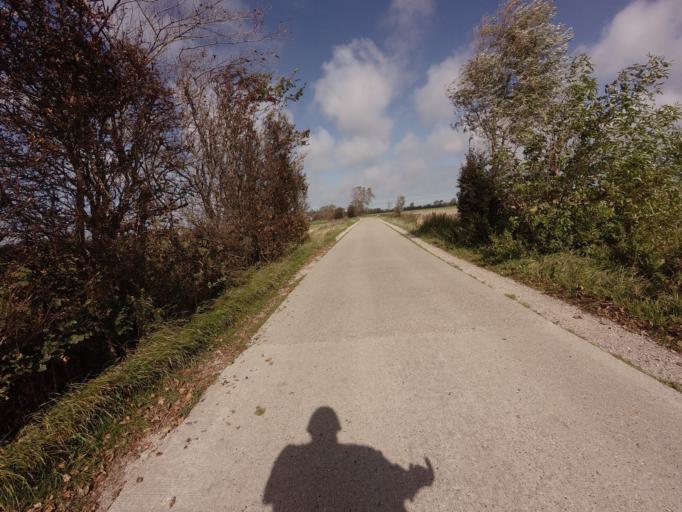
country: NL
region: Zeeland
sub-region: Gemeente Middelburg
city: Middelburg
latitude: 51.5413
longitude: 3.5206
